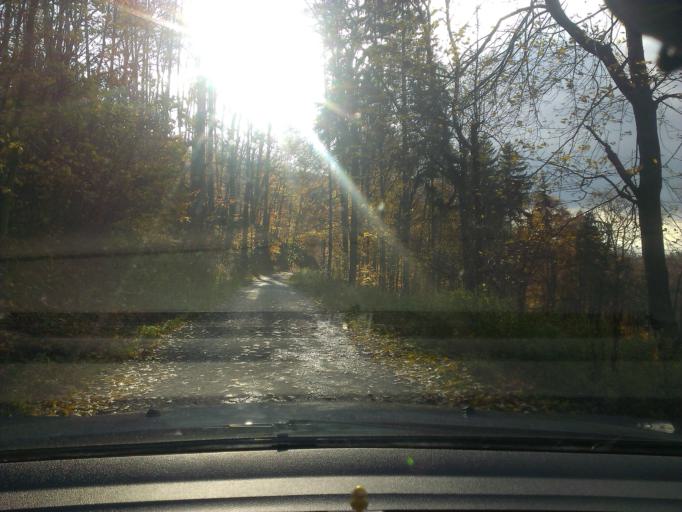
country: SK
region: Trnavsky
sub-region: Okres Trnava
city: Piestany
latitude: 48.6150
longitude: 17.9577
